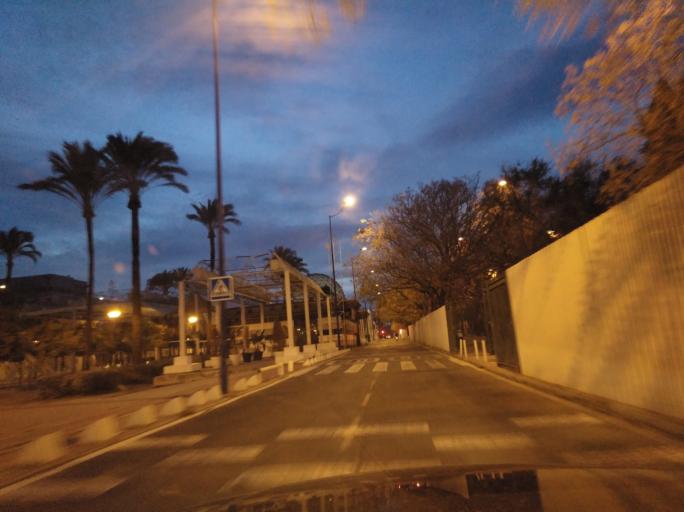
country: ES
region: Andalusia
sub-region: Provincia de Sevilla
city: Camas
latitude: 37.4060
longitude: -6.0043
